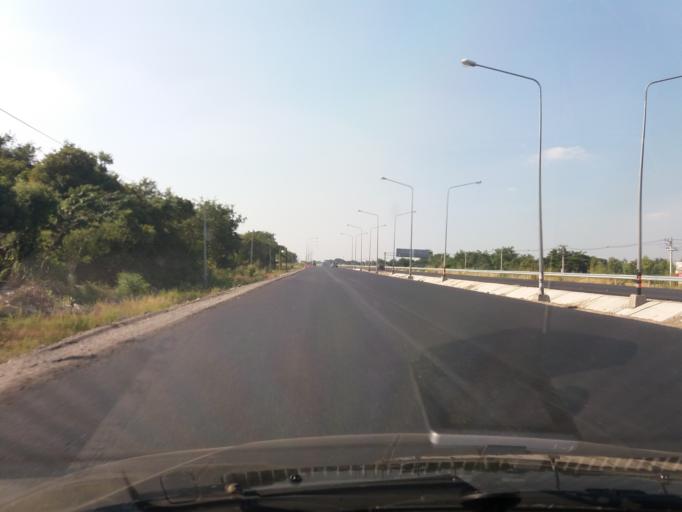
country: TH
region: Nakhon Sawan
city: Krok Phra
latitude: 15.6220
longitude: 100.1140
